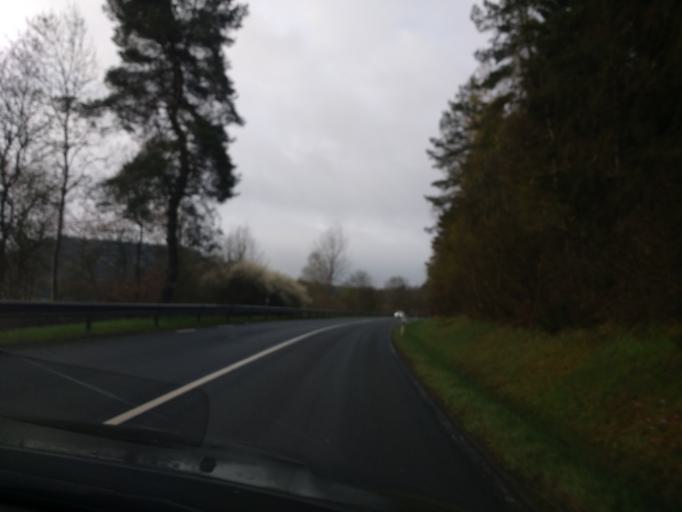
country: DE
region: Rheinland-Pfalz
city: Dohm-Lammersdorf
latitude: 50.2536
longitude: 6.6592
